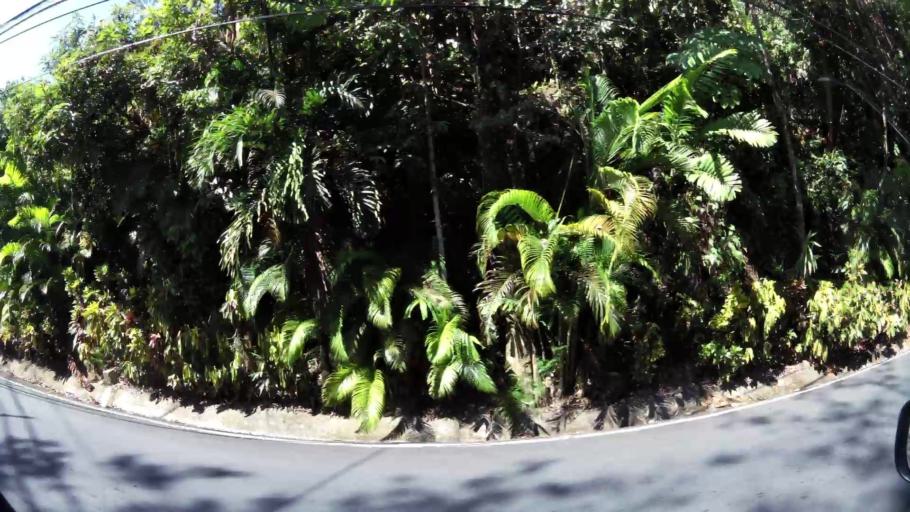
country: CR
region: Puntarenas
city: Quepos
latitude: 9.3978
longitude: -84.1546
